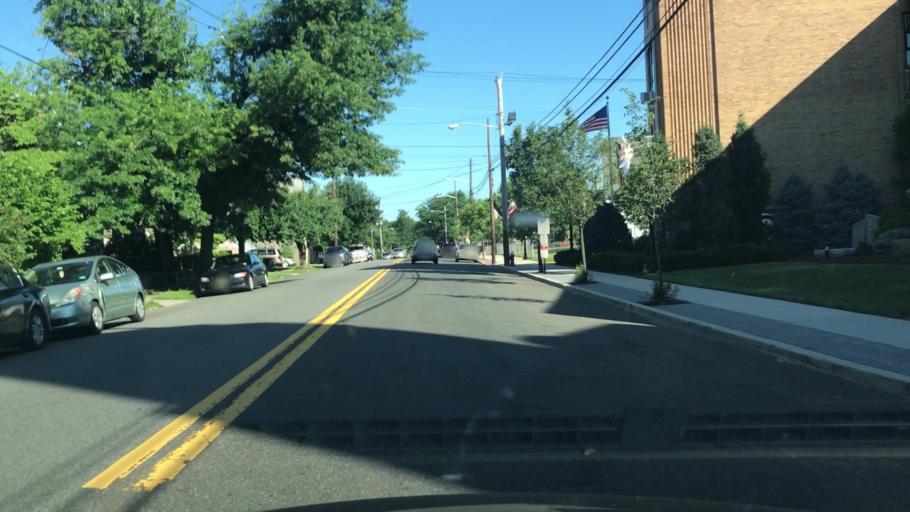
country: US
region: New Jersey
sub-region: Bergen County
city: Wallington
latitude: 40.8511
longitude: -74.1157
